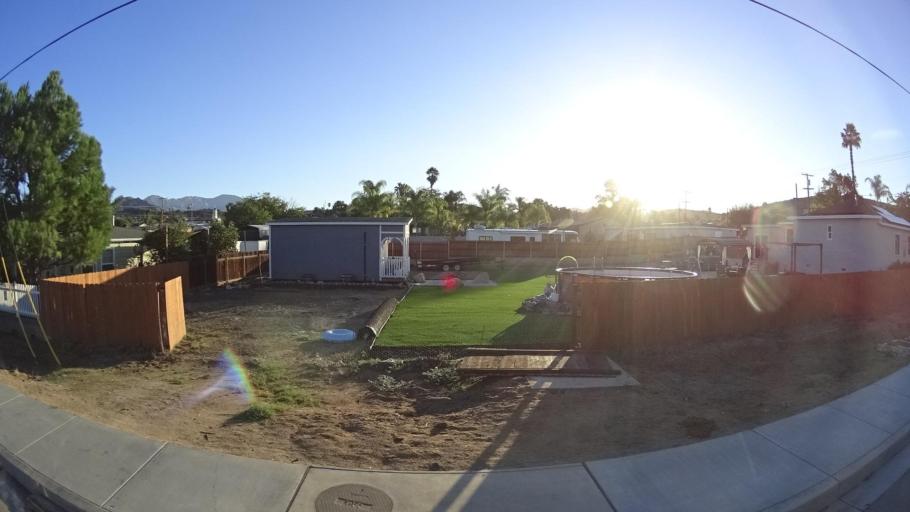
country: US
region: California
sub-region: San Diego County
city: Lakeside
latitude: 32.8567
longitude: -116.9122
